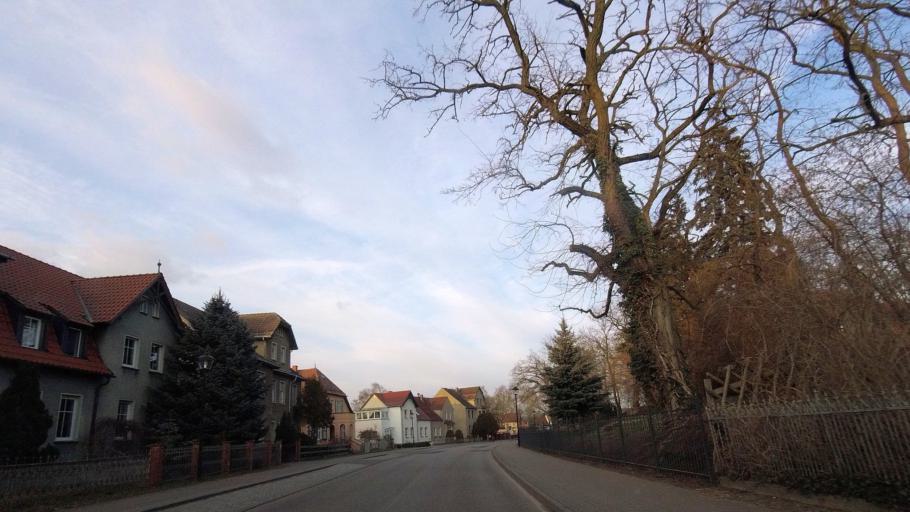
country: DE
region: Brandenburg
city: Niemegk
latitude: 52.0791
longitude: 12.6901
